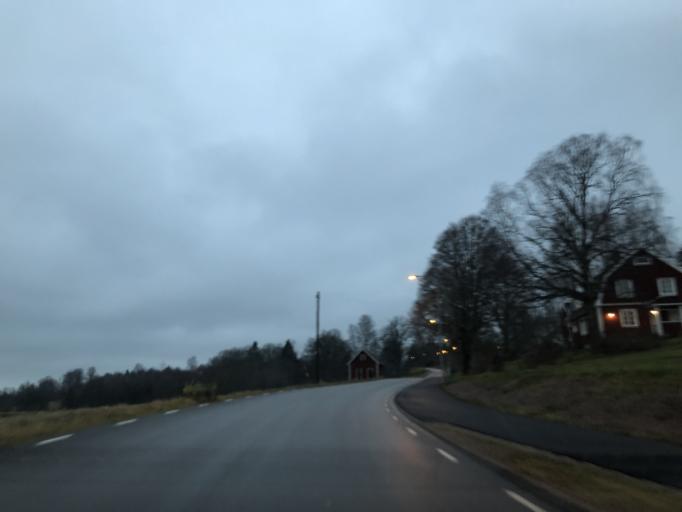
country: SE
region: Vaestra Goetaland
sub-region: Ulricehamns Kommun
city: Ulricehamn
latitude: 57.8429
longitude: 13.2781
